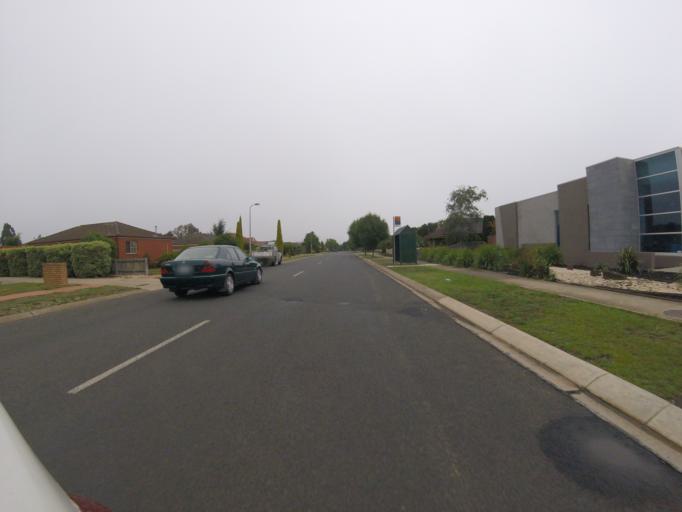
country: AU
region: Victoria
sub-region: Ballarat North
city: Newington
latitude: -37.5466
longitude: 143.7949
